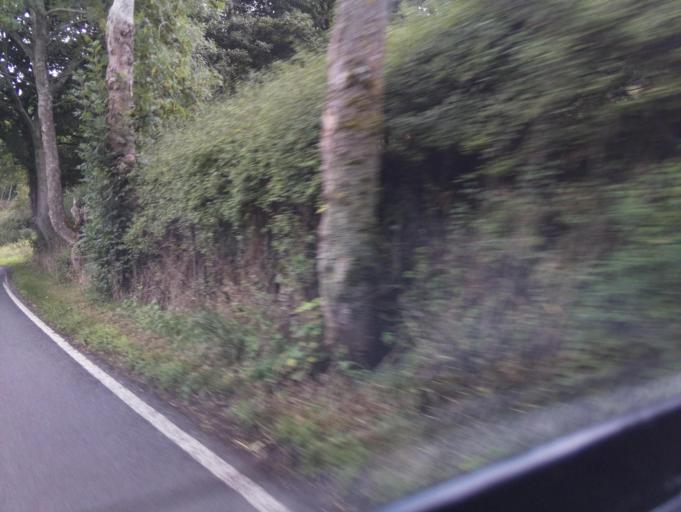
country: GB
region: England
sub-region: North Yorkshire
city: Leyburn
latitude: 54.3965
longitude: -1.8264
